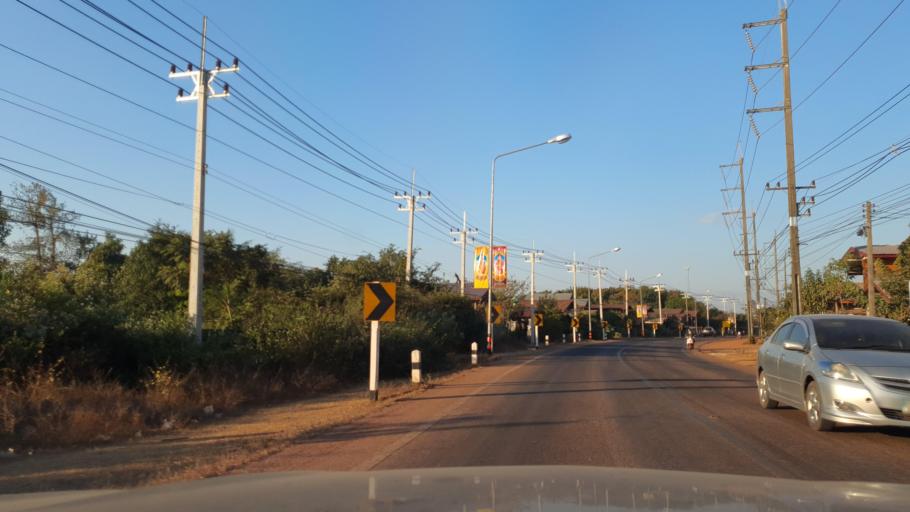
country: TH
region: Nakhon Phanom
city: Si Songkhram
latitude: 17.5850
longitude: 104.2333
